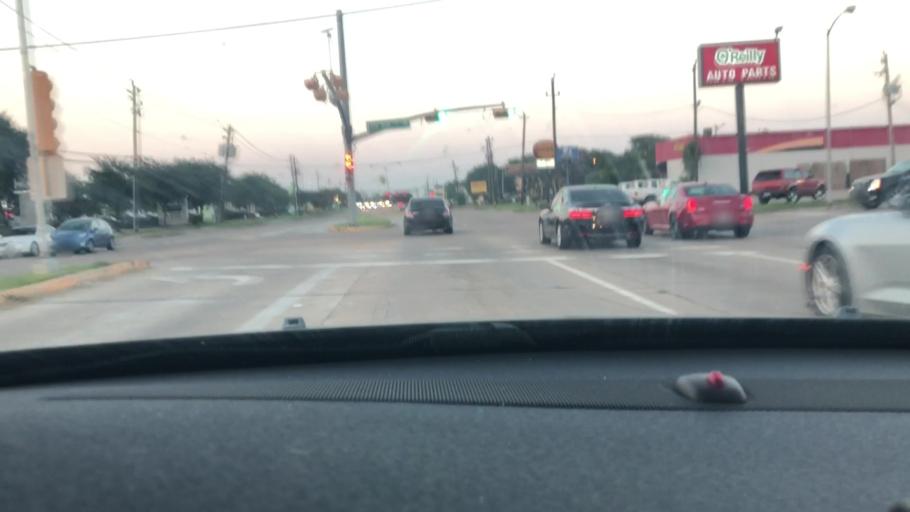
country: US
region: Texas
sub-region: Harris County
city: Webster
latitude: 29.5465
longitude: -95.1316
